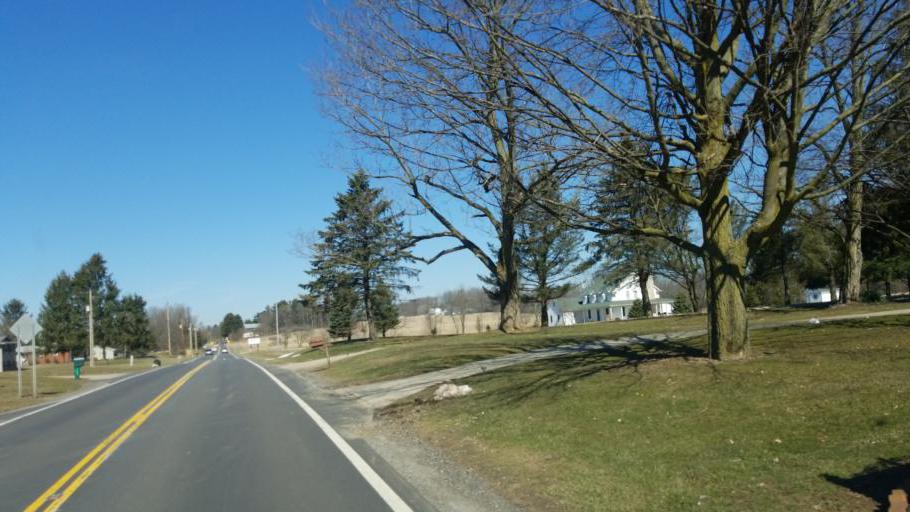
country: US
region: Ohio
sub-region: Richland County
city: Lexington
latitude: 40.6602
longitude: -82.5524
